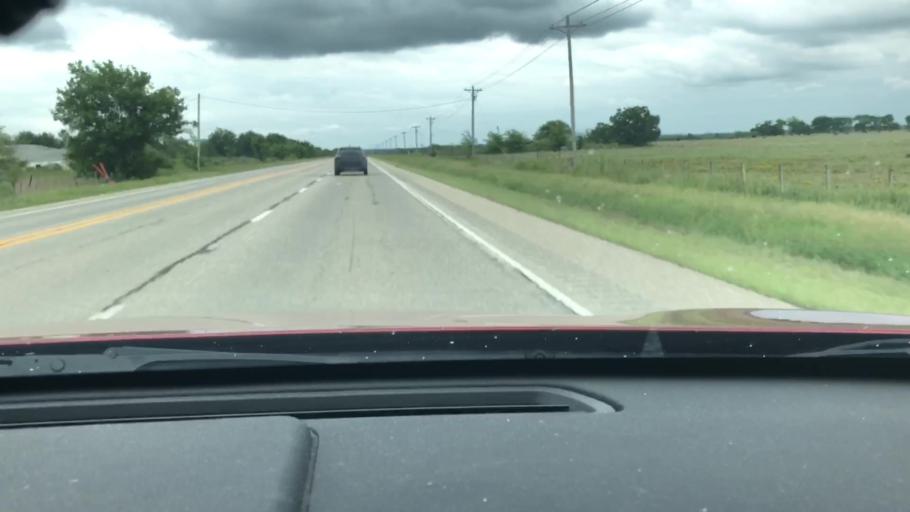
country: US
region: Arkansas
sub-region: Lafayette County
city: Lewisville
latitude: 33.4125
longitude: -93.7931
